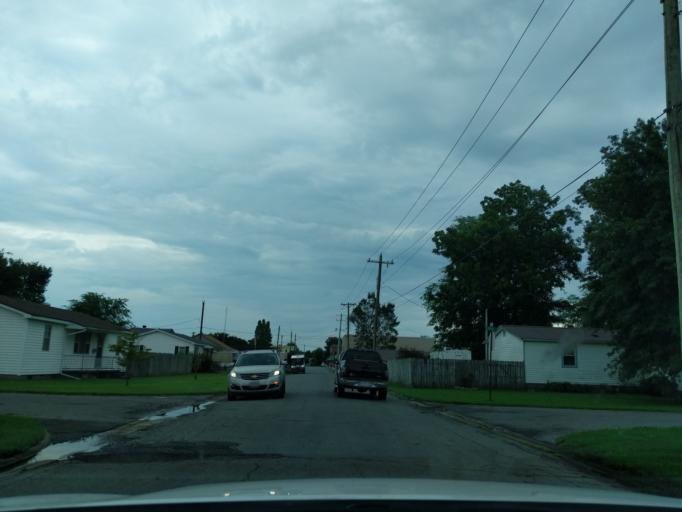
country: US
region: Missouri
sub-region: New Madrid County
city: New Madrid
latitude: 36.5848
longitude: -89.5306
